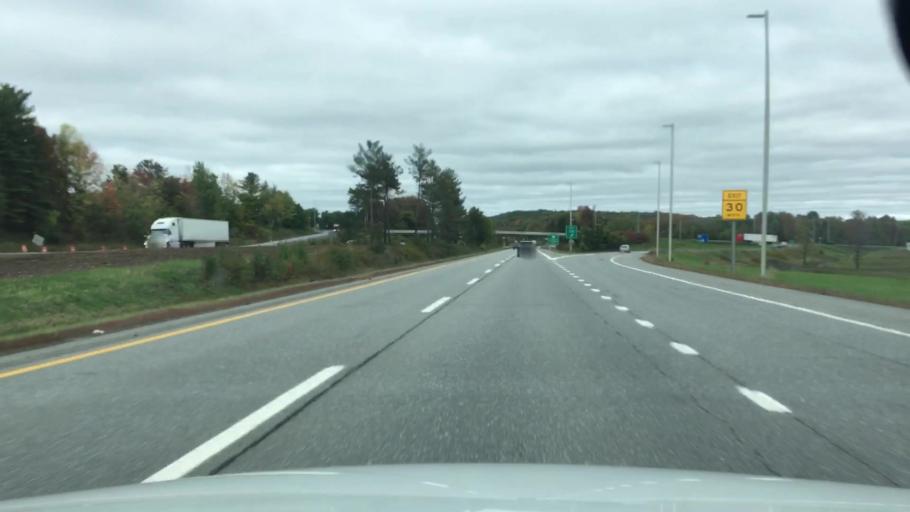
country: US
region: Maine
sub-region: Somerset County
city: Fairfield
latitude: 44.5911
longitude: -69.6180
